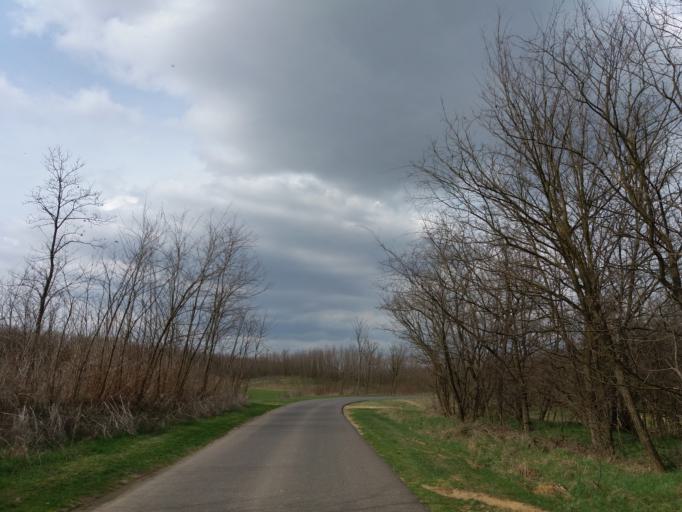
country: HU
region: Szabolcs-Szatmar-Bereg
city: Petnehaza
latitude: 48.0697
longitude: 22.0454
